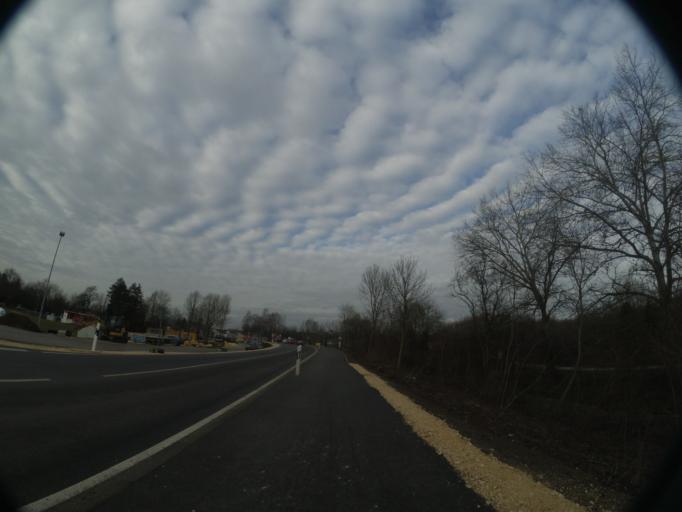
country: DE
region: Baden-Wuerttemberg
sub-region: Tuebingen Region
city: Erbach
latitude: 48.3525
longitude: 9.9223
